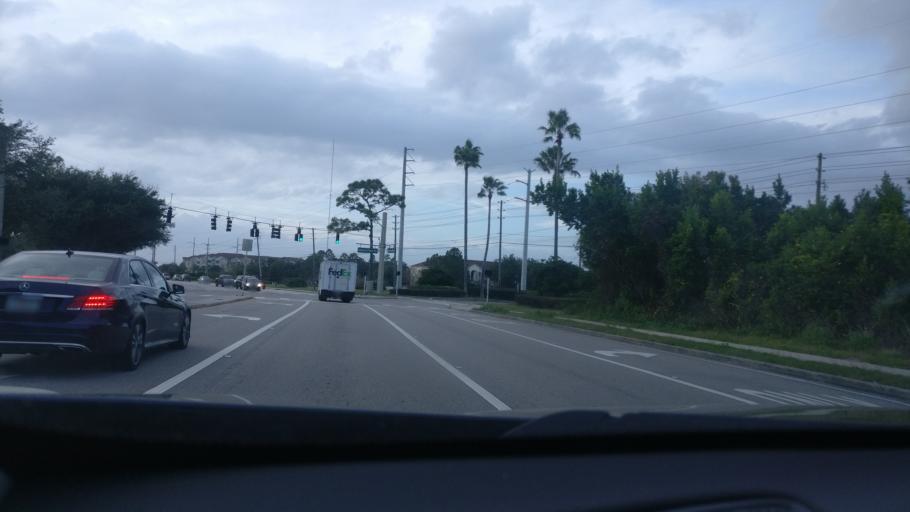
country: US
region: Florida
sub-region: Volusia County
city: DeBary
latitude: 28.9117
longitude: -81.2950
